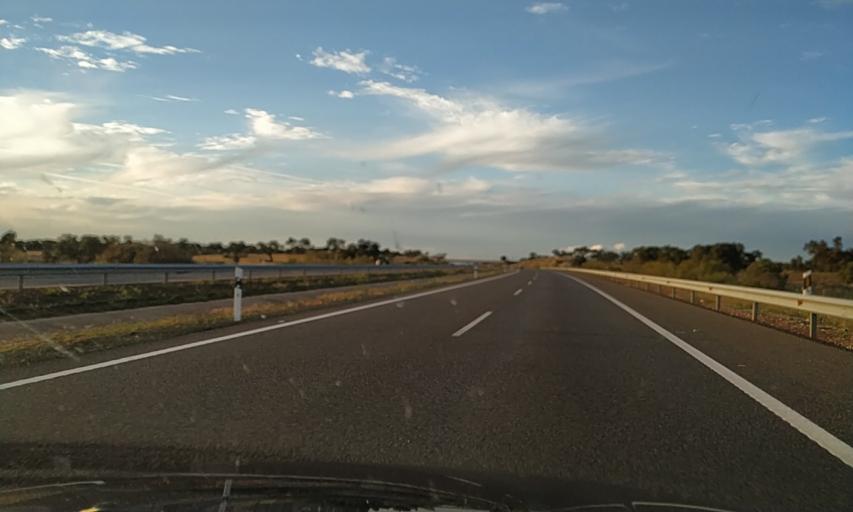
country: ES
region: Extremadura
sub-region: Provincia de Badajoz
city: Aljucen
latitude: 39.0140
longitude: -6.3298
